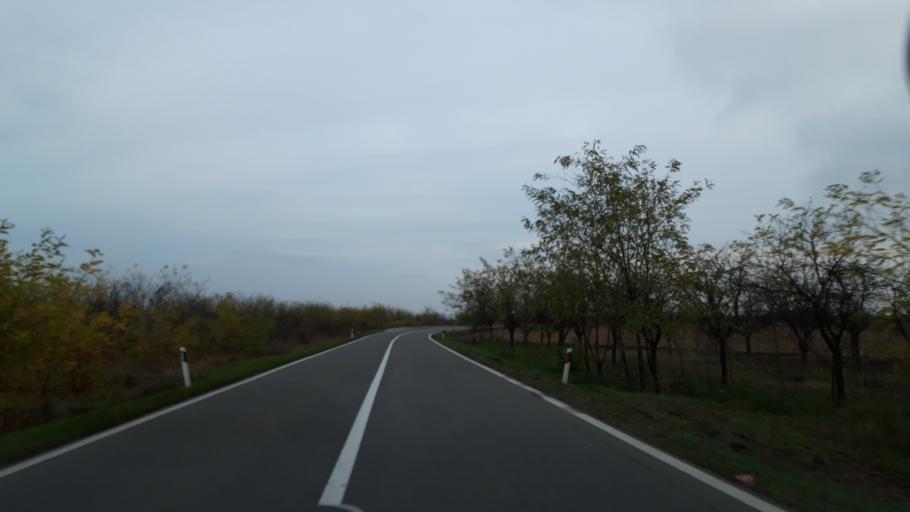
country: RS
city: Sanad
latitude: 45.9650
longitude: 20.1282
